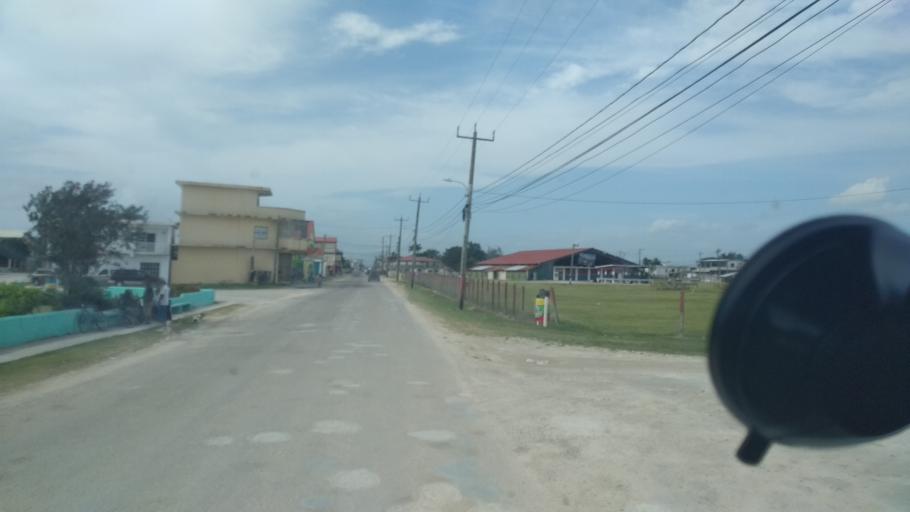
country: BZ
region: Corozal
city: Corozal
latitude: 18.3962
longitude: -88.3816
